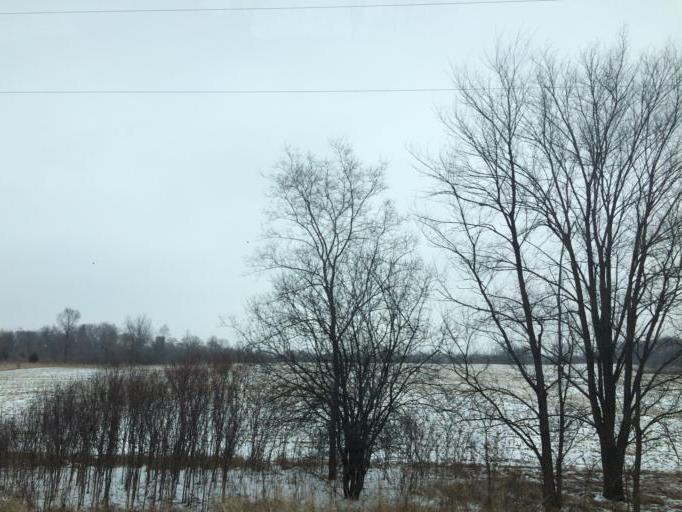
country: US
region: Illinois
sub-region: McHenry County
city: Woodstock
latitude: 42.2661
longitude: -88.4330
